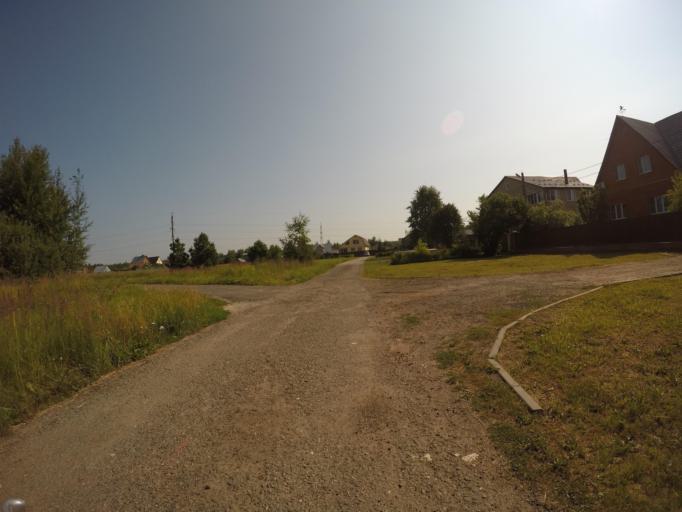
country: RU
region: Moskovskaya
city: Rechitsy
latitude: 55.6136
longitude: 38.5418
